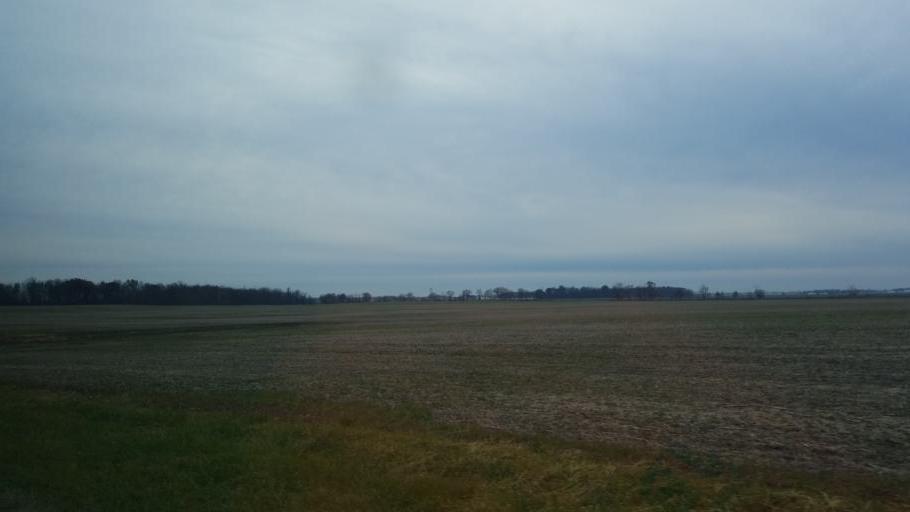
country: US
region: Indiana
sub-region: Adams County
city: Berne
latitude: 40.6722
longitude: -84.8595
